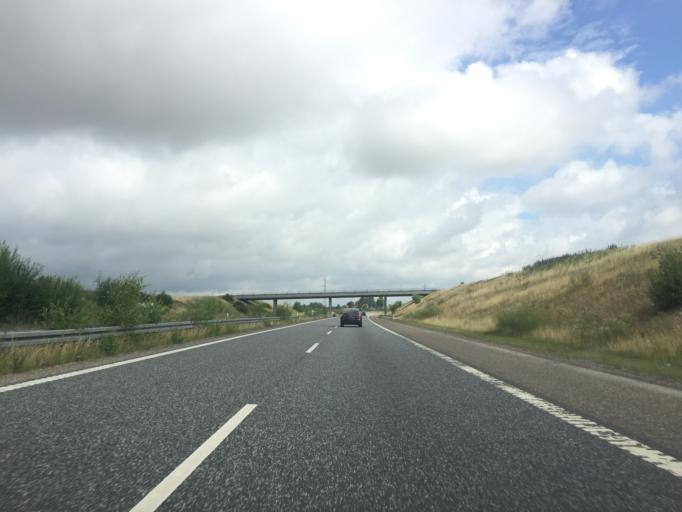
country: DK
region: South Denmark
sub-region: Svendborg Kommune
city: Svendborg
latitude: 55.1123
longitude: 10.5615
